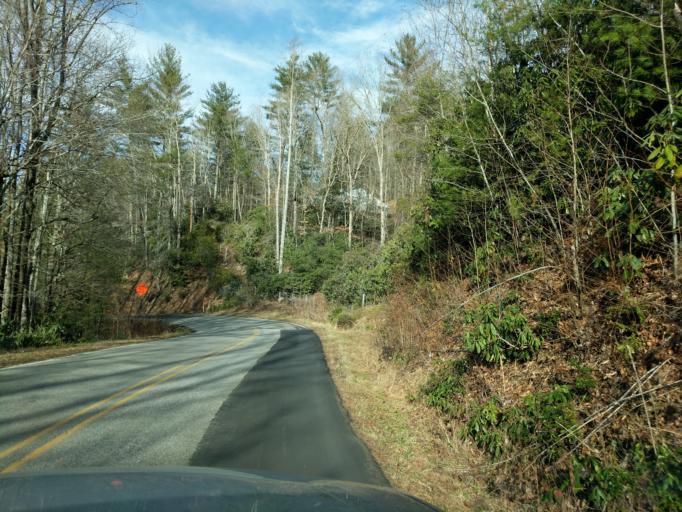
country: US
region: North Carolina
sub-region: Haywood County
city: Cove Creek
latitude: 35.6629
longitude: -83.0117
